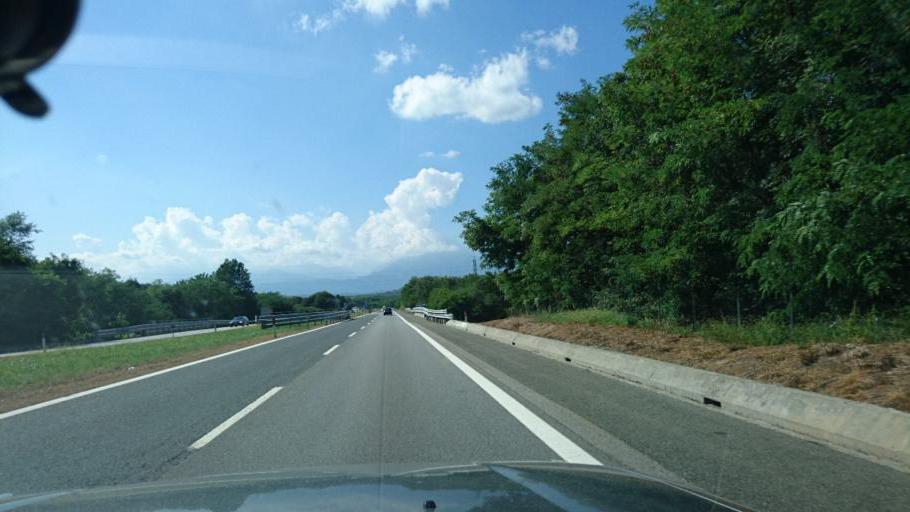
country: IT
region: Piedmont
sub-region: Provincia di Torino
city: Settimo Rottaro
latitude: 45.4112
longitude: 8.0058
